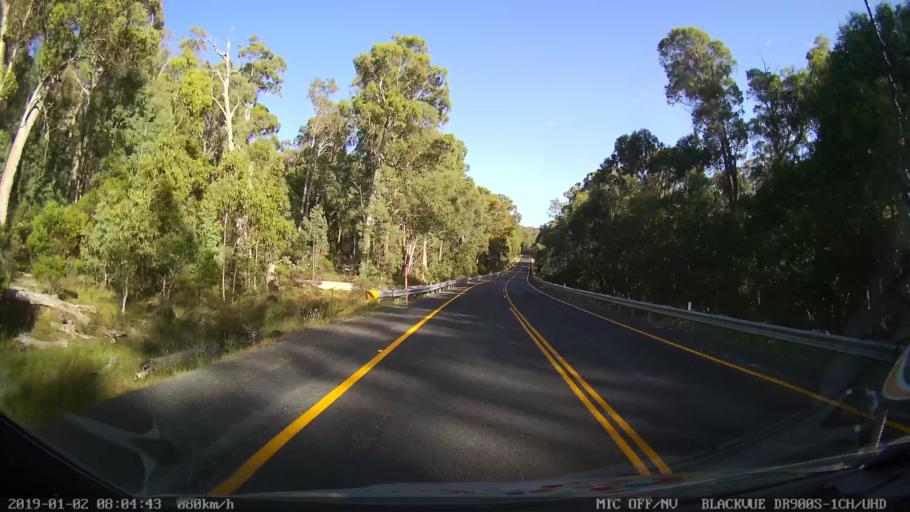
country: AU
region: New South Wales
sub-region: Tumut Shire
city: Tumut
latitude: -35.6594
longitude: 148.3921
